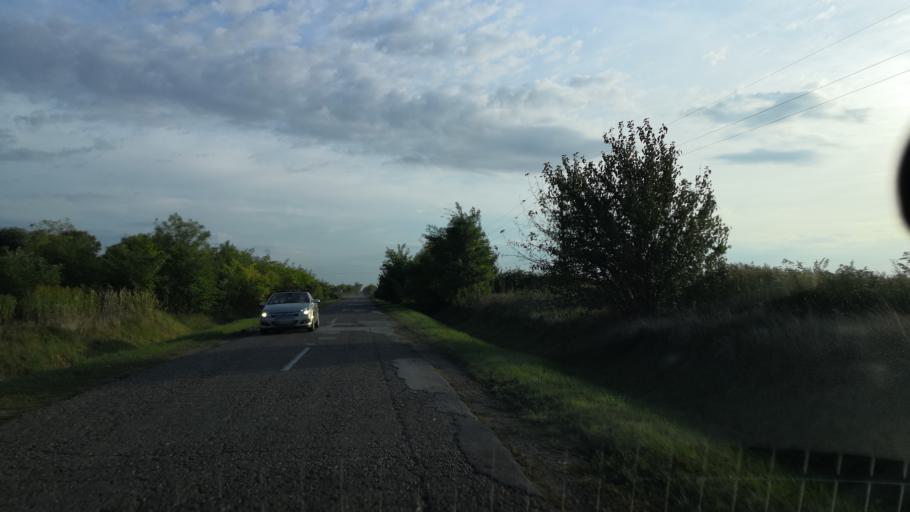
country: RS
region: Autonomna Pokrajina Vojvodina
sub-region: Sremski Okrug
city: Stara Pazova
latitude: 45.0289
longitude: 20.1718
